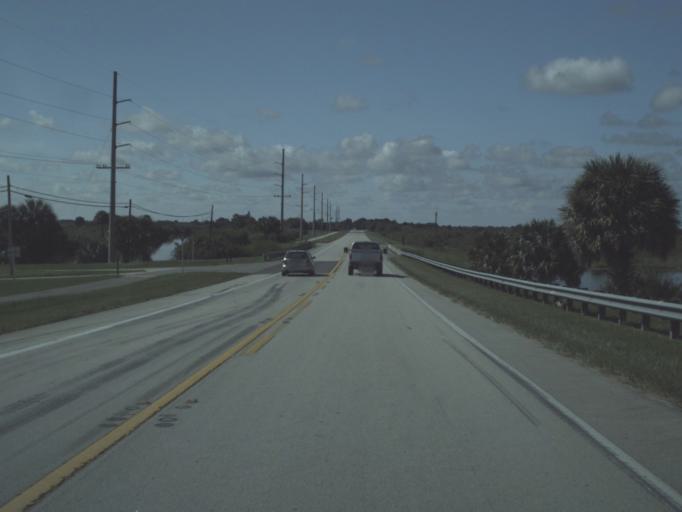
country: US
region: Florida
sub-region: Glades County
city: Moore Haven
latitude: 26.9694
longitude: -81.1185
